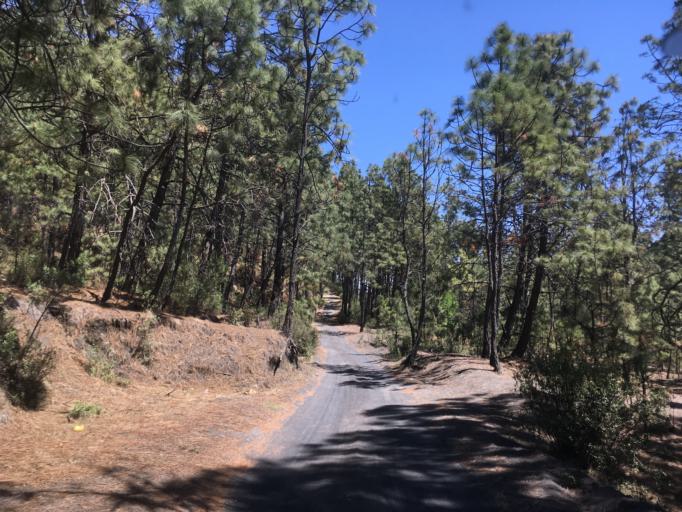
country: MX
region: Michoacan
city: Angahuan
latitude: 19.4684
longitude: -102.2401
